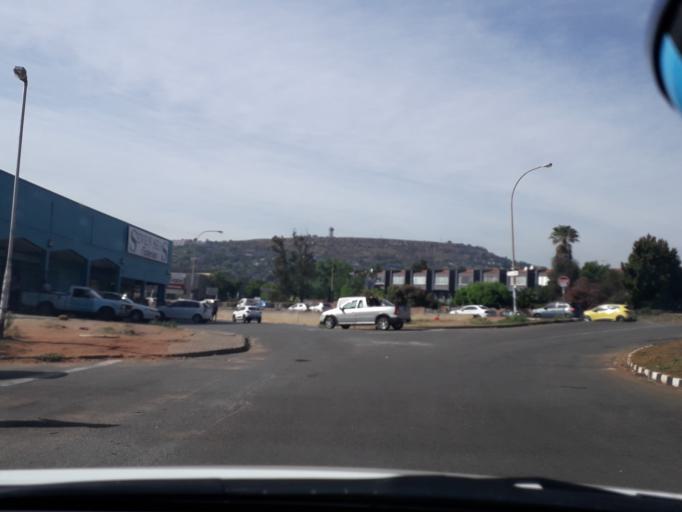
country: ZA
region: Gauteng
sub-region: City of Johannesburg Metropolitan Municipality
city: Roodepoort
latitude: -26.1252
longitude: 27.9662
